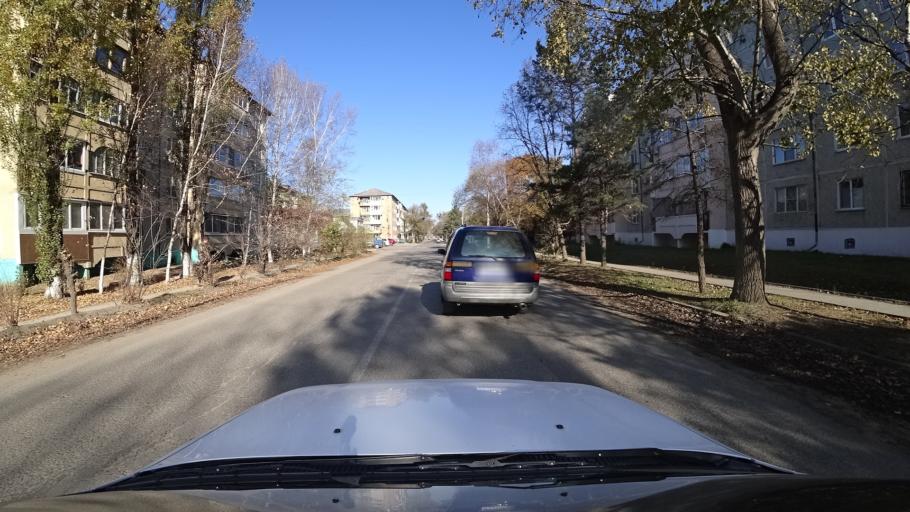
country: RU
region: Primorskiy
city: Dal'nerechensk
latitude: 45.9354
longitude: 133.7336
